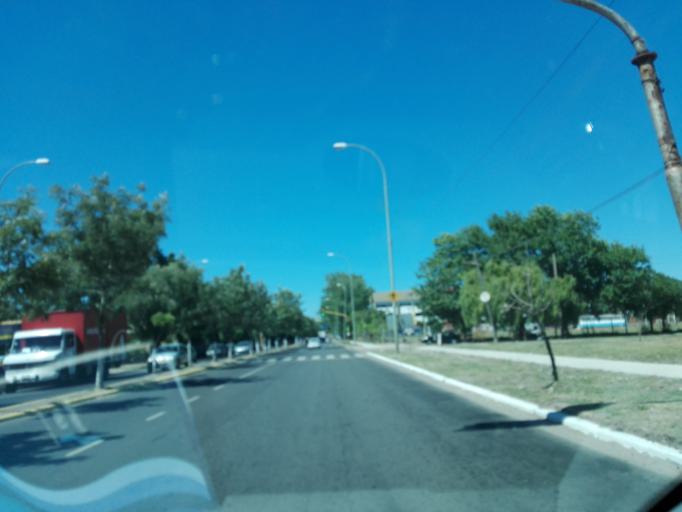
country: AR
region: Buenos Aires
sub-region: Partido de La Plata
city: La Plata
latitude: -34.9025
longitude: -57.9234
